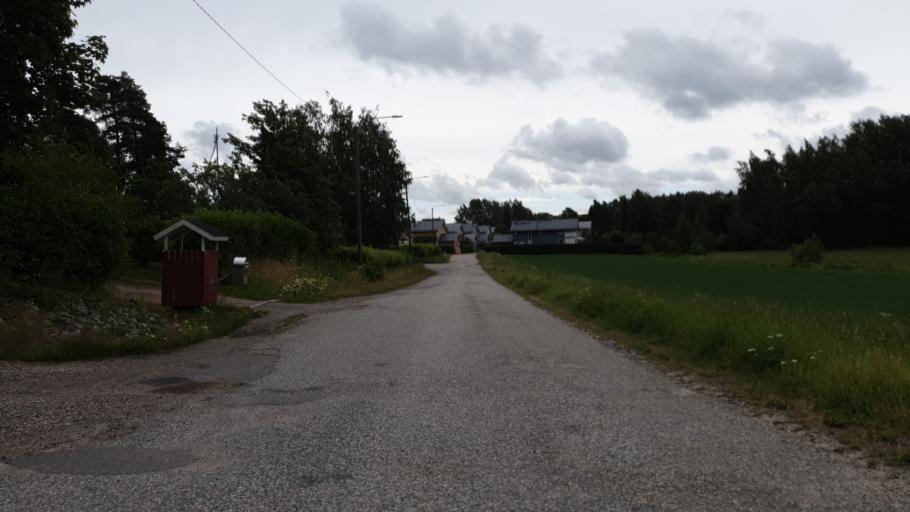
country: FI
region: Uusimaa
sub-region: Helsinki
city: Teekkarikylae
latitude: 60.2782
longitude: 24.9021
